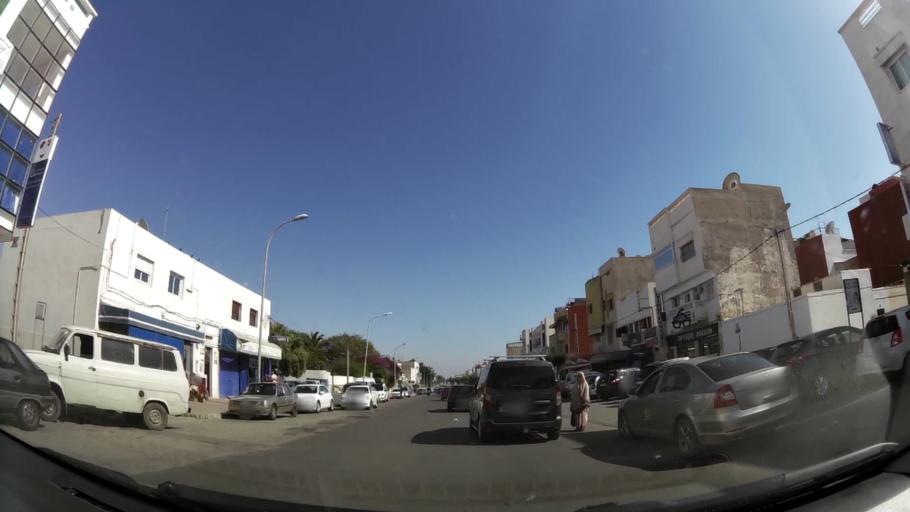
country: MA
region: Souss-Massa-Draa
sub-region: Agadir-Ida-ou-Tnan
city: Agadir
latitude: 30.4150
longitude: -9.5885
